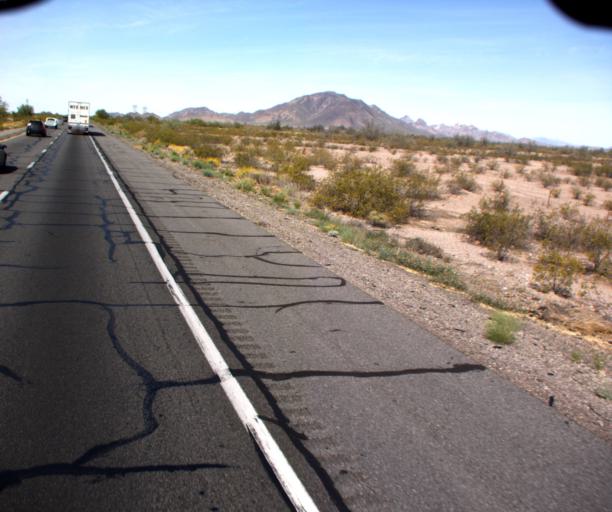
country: US
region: Arizona
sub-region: Maricopa County
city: Buckeye
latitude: 33.5112
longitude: -113.0126
